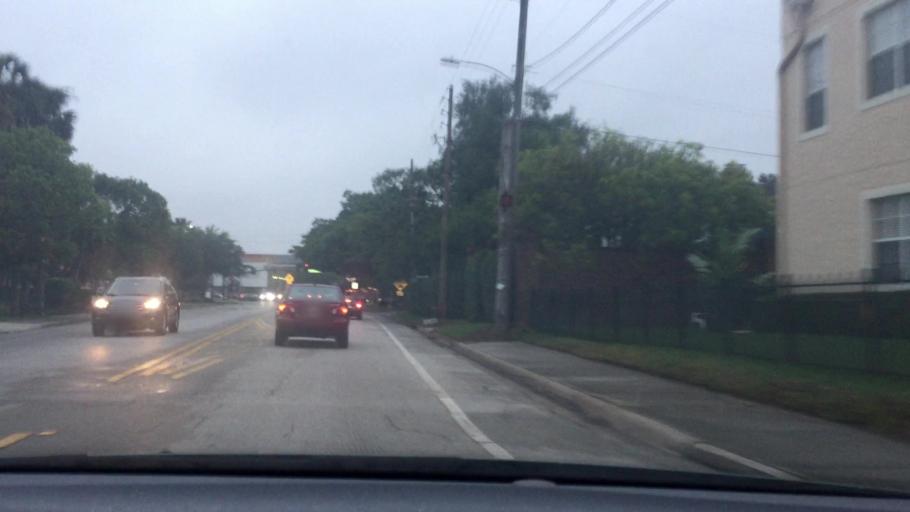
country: US
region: Florida
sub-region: Orange County
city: Fairview Shores
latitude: 28.5821
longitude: -81.3878
